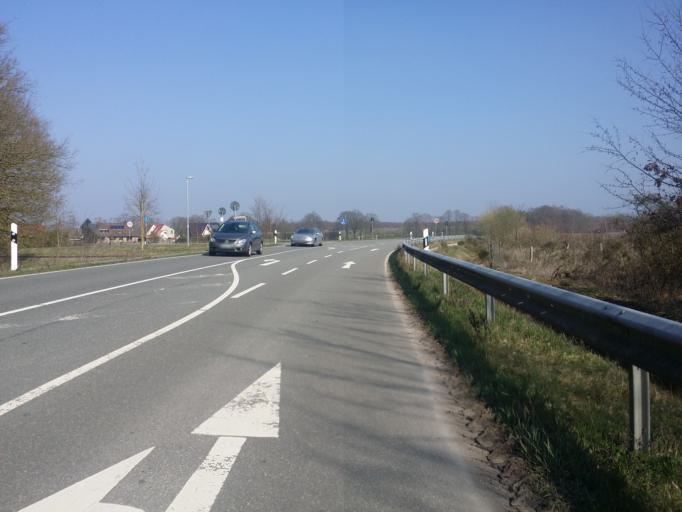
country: DE
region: Lower Saxony
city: Kirchseelte
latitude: 53.0133
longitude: 8.6877
